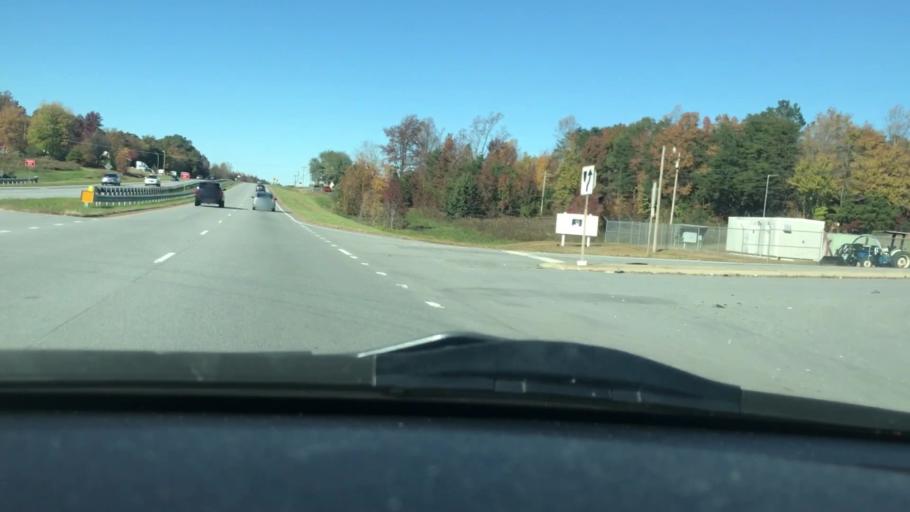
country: US
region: North Carolina
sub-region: Rockingham County
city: Madison
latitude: 36.3210
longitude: -79.9447
